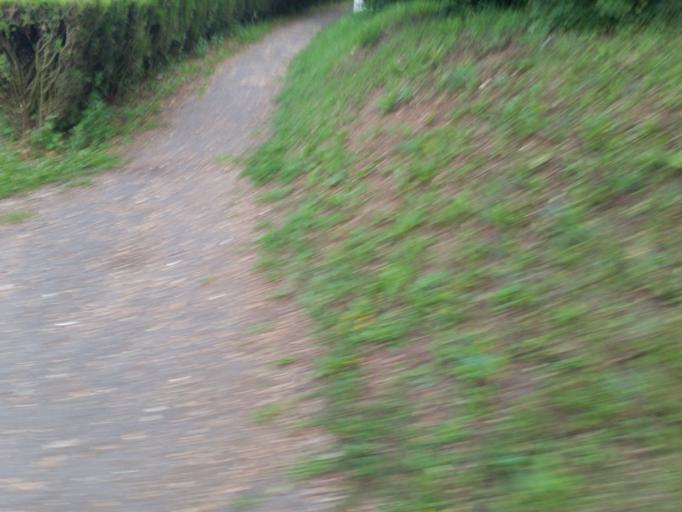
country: RO
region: Cluj
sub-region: Municipiul Cluj-Napoca
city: Cluj-Napoca
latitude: 46.7758
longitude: 23.5822
